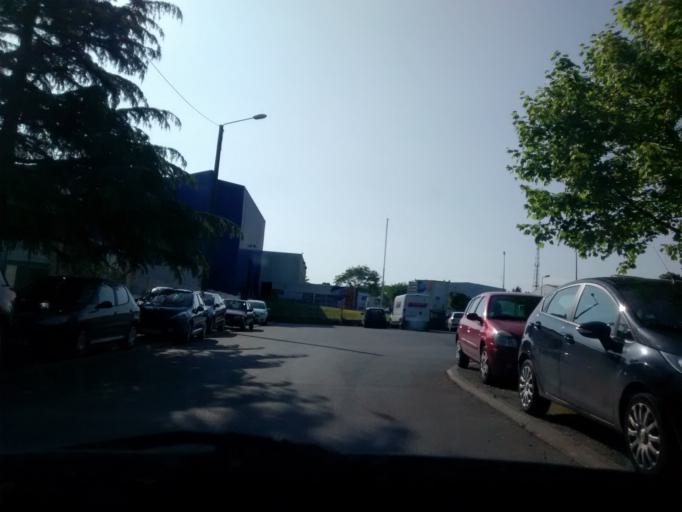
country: FR
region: Brittany
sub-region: Departement d'Ille-et-Vilaine
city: Chantepie
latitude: 48.1046
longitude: -1.6245
